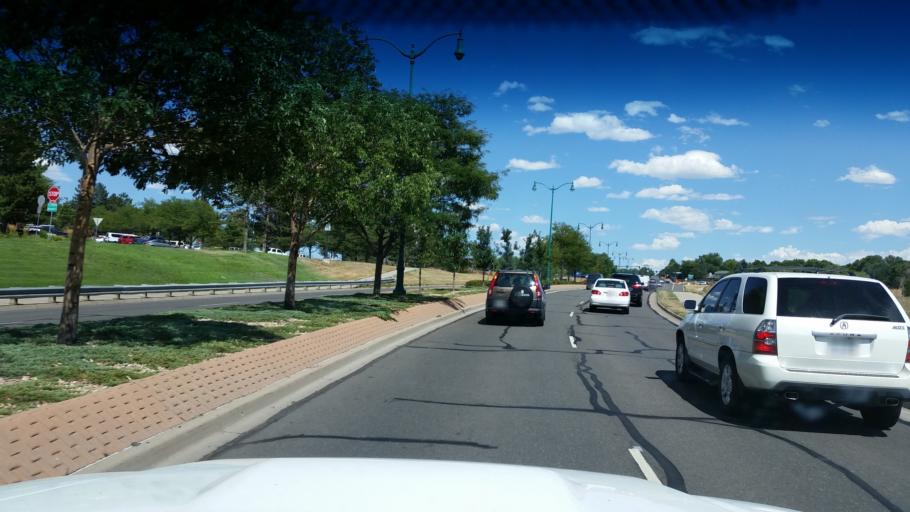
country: US
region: Colorado
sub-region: Broomfield County
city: Broomfield
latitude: 39.8852
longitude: -105.0576
